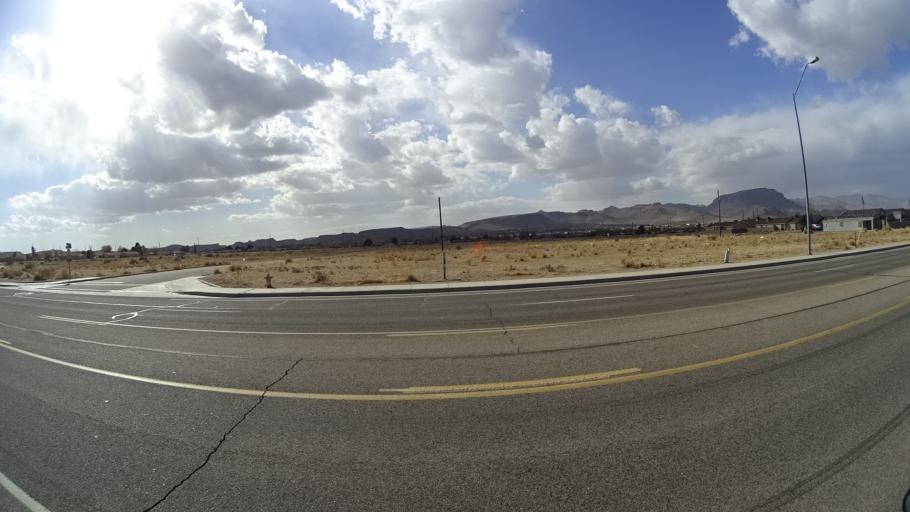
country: US
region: Arizona
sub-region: Mohave County
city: New Kingman-Butler
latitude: 35.2306
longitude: -114.0114
